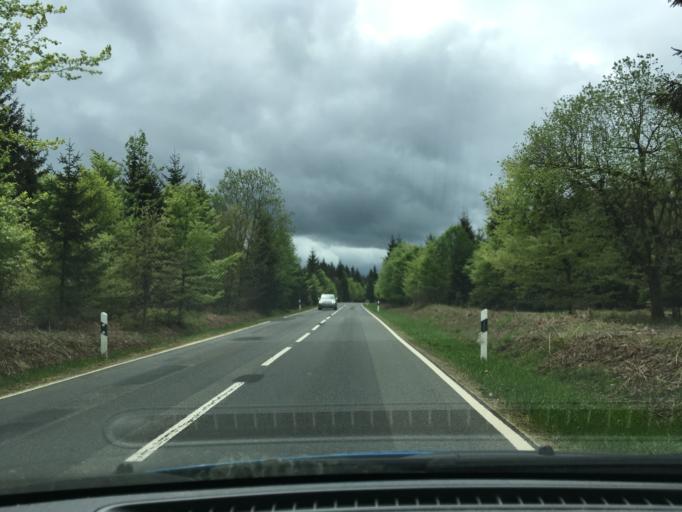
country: DE
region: Lower Saxony
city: Heinade
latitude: 51.7707
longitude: 9.5738
